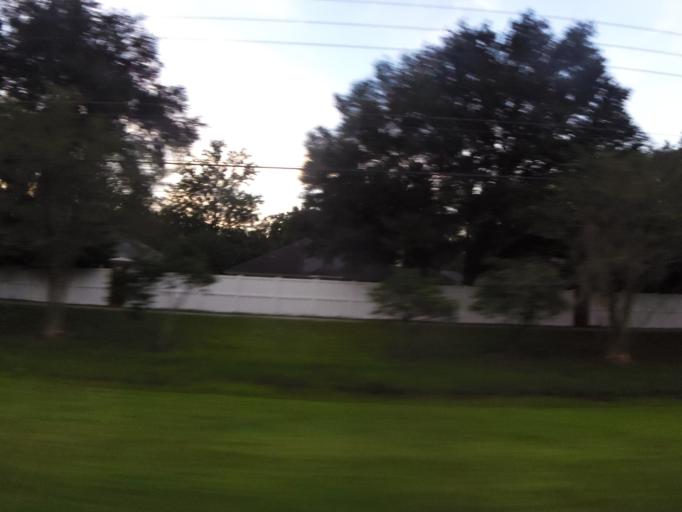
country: US
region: Florida
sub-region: Saint Johns County
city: Fruit Cove
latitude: 30.1194
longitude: -81.6141
